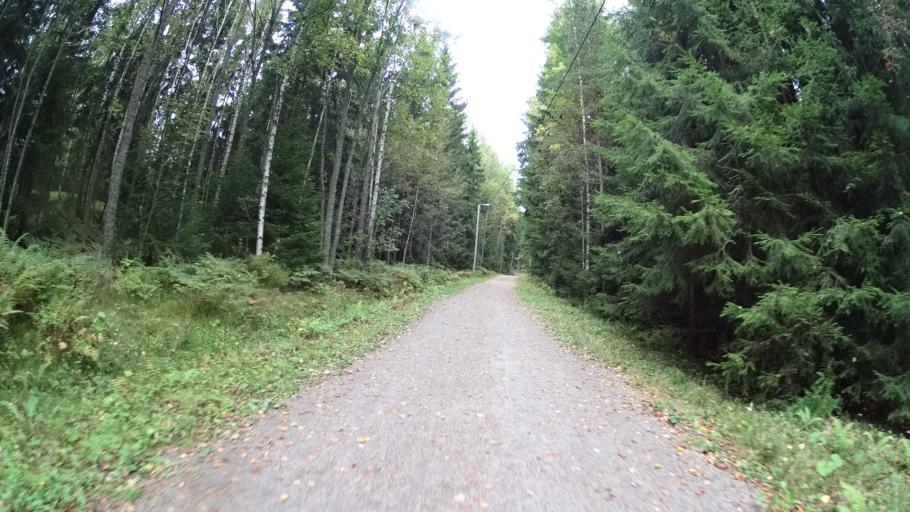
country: FI
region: Uusimaa
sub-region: Helsinki
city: Kauniainen
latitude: 60.1907
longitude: 24.7073
